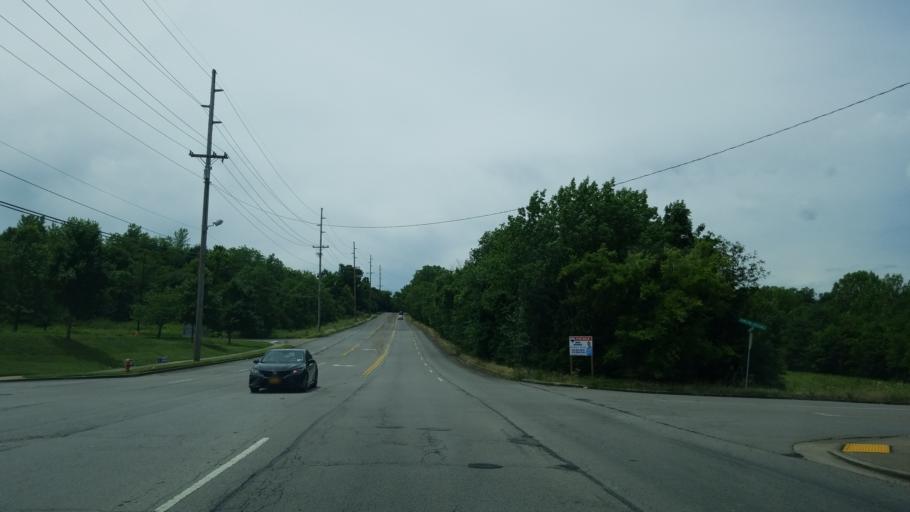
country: US
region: Tennessee
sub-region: Rutherford County
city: La Vergne
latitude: 36.0629
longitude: -86.6306
